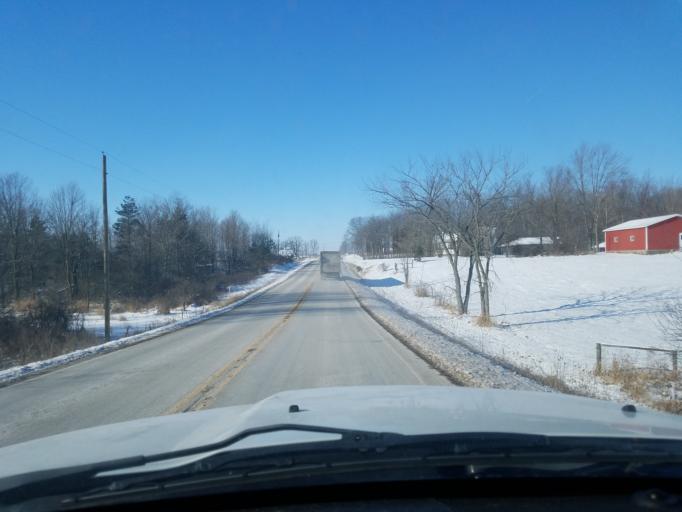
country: US
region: Indiana
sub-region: Noble County
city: Avilla
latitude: 41.3945
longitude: -85.2583
